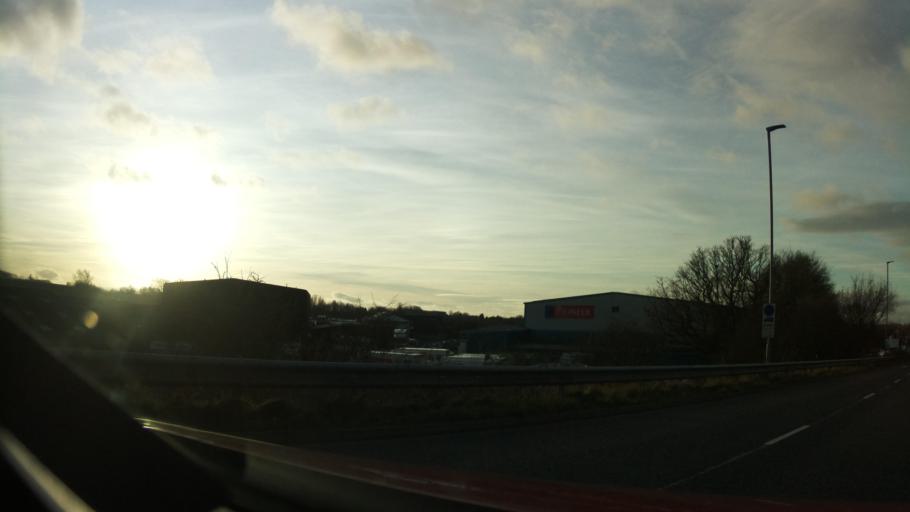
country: GB
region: England
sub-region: Cumbria
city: Scotby
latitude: 54.8953
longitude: -2.8911
